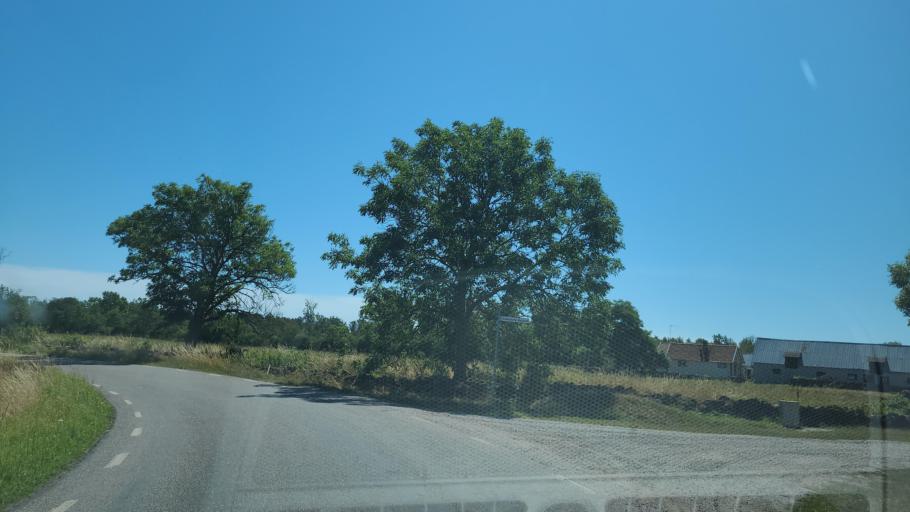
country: SE
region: Kalmar
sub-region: Borgholms Kommun
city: Borgholm
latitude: 56.7441
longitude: 16.6670
